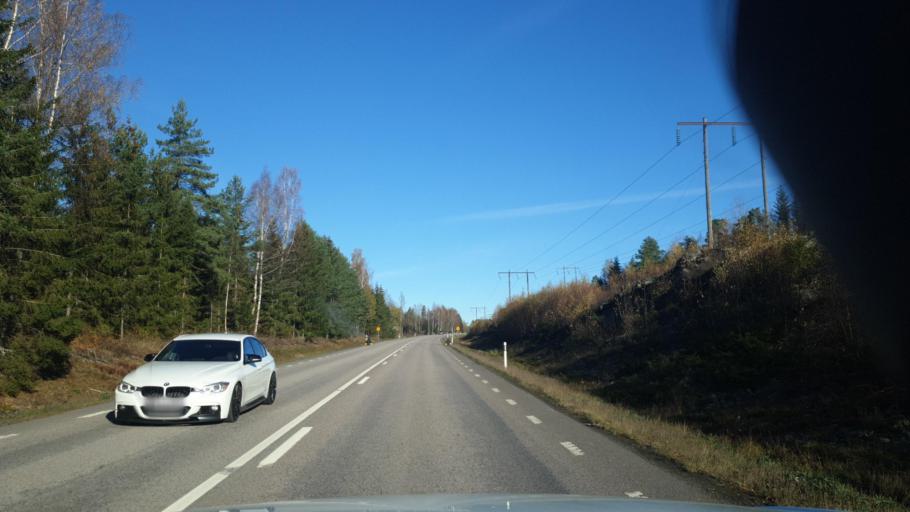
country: SE
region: Vaermland
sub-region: Karlstads Kommun
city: Valberg
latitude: 59.4086
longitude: 13.1819
